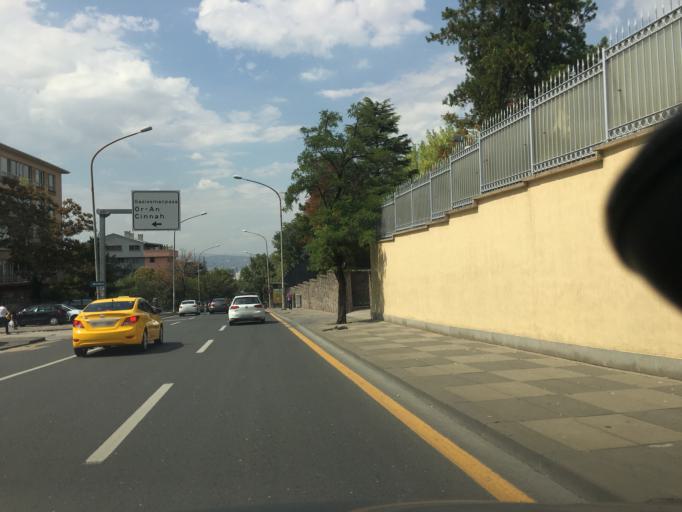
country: TR
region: Ankara
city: Cankaya
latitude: 39.8971
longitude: 32.8617
